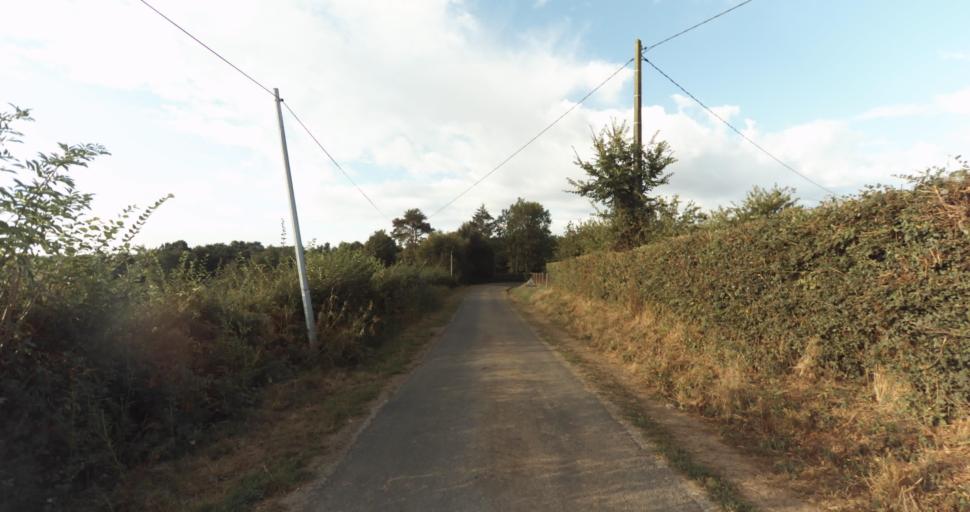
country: FR
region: Lower Normandy
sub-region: Departement de l'Orne
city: Vimoutiers
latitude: 48.9377
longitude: 0.2499
